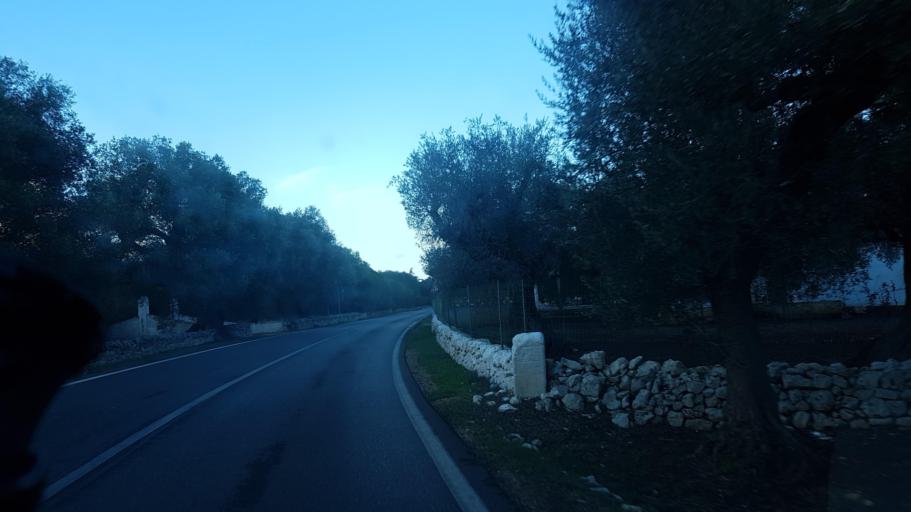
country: IT
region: Apulia
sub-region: Provincia di Brindisi
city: San Michele Salentino
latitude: 40.6564
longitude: 17.6023
